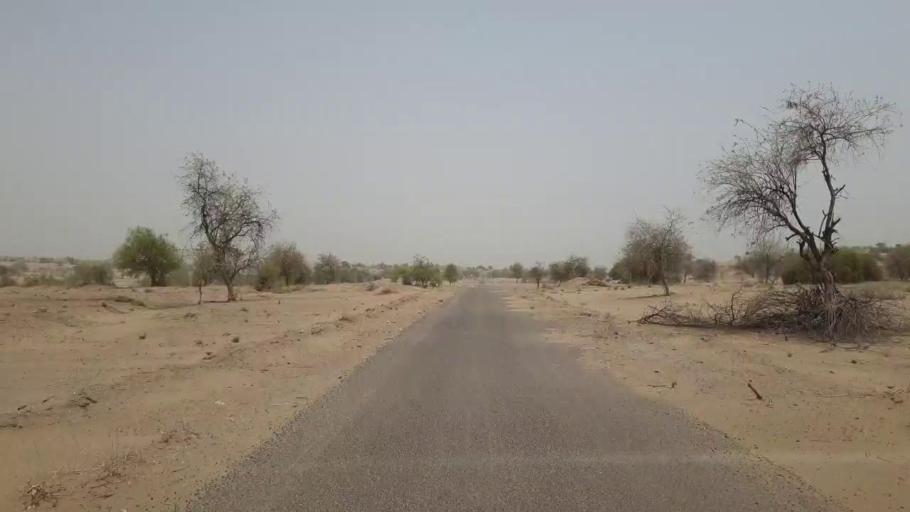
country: PK
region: Sindh
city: Islamkot
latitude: 24.8079
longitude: 70.5360
